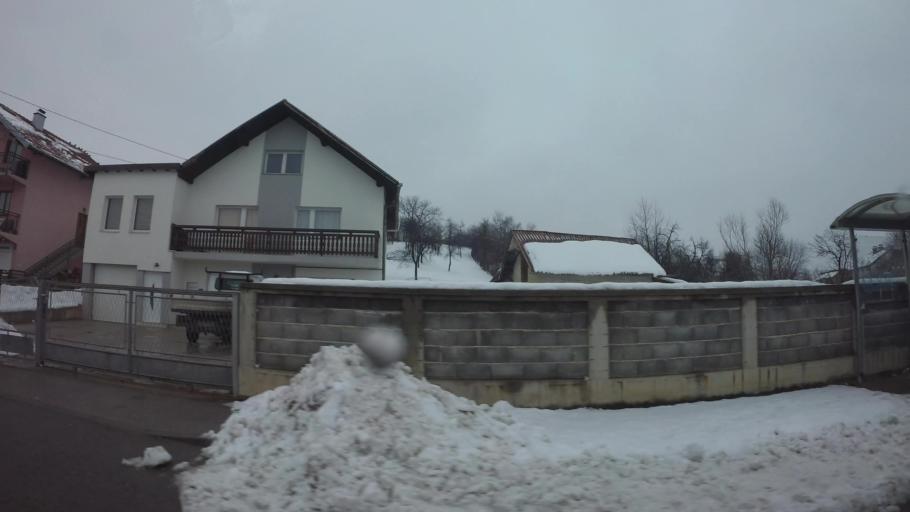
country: BA
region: Federation of Bosnia and Herzegovina
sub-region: Kanton Sarajevo
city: Sarajevo
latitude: 43.8493
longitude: 18.2798
